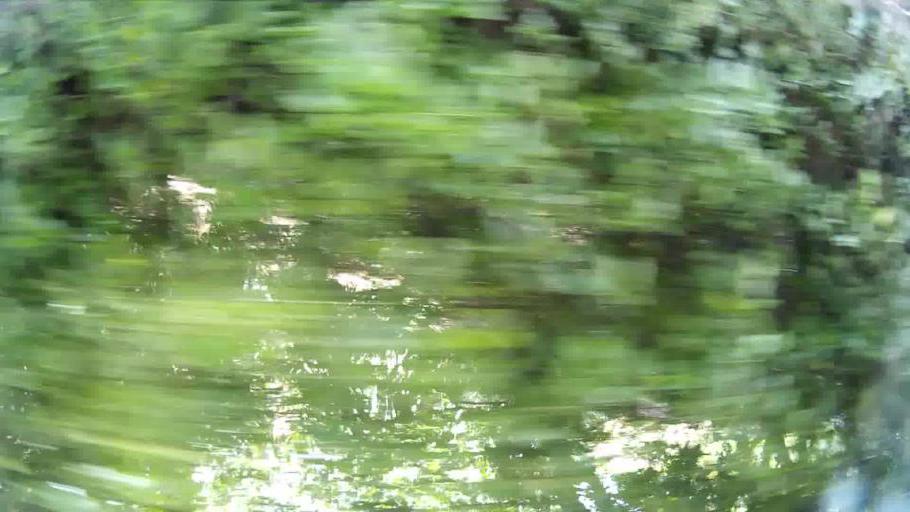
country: CO
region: Risaralda
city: La Virginia
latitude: 4.9413
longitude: -75.8424
